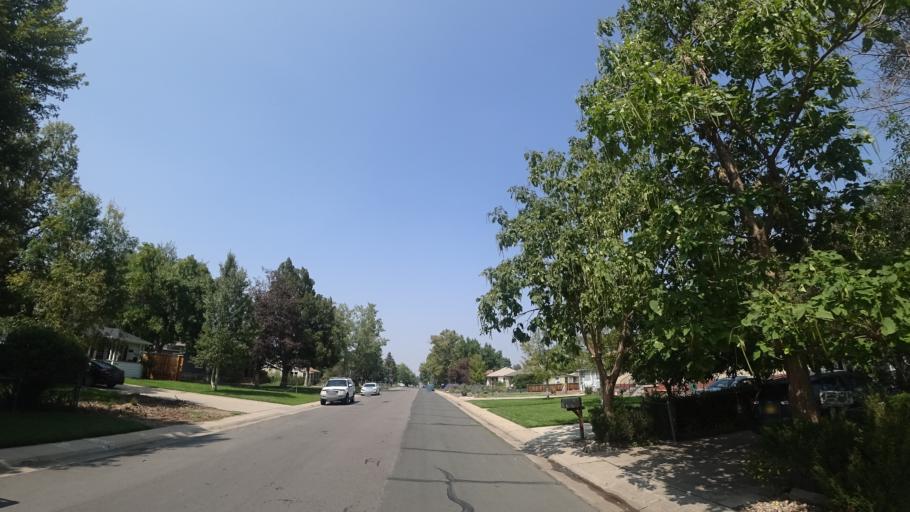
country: US
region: Colorado
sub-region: Arapahoe County
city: Englewood
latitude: 39.6283
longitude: -104.9949
